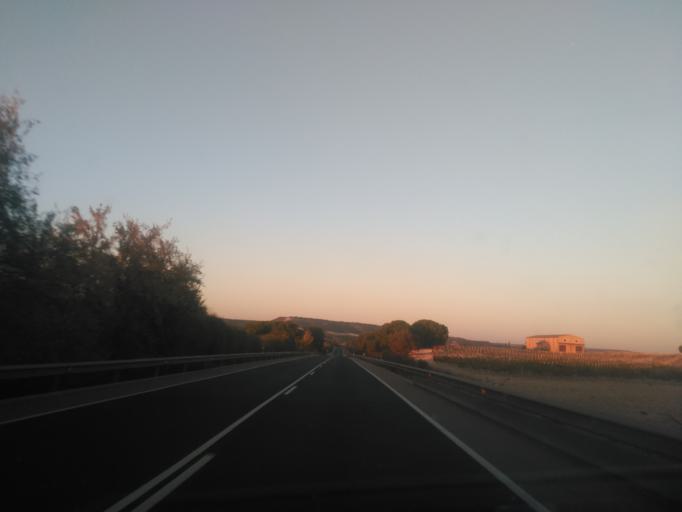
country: ES
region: Castille and Leon
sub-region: Provincia de Valladolid
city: Quintanilla de Onesimo
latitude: 41.6207
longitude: -4.3562
